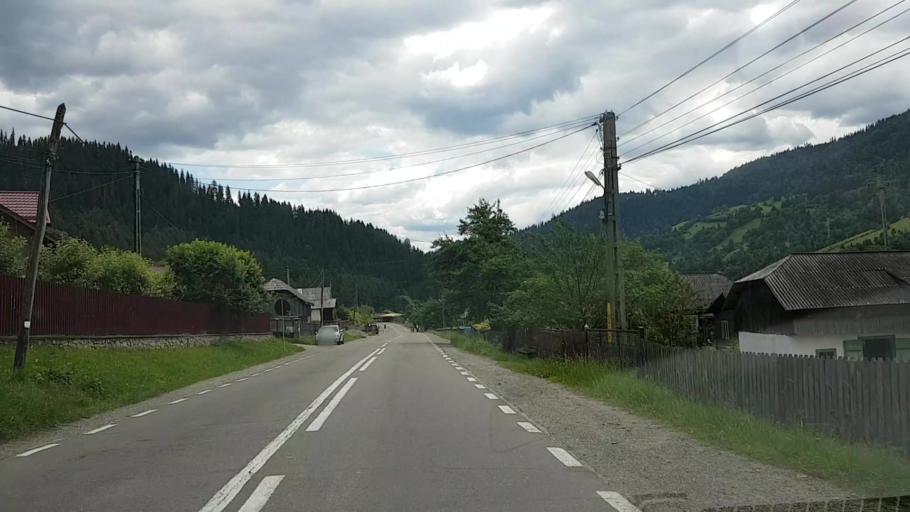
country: RO
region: Neamt
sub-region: Comuna Poiana Teiului
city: Poiana Teiului
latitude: 47.1304
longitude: 25.9007
